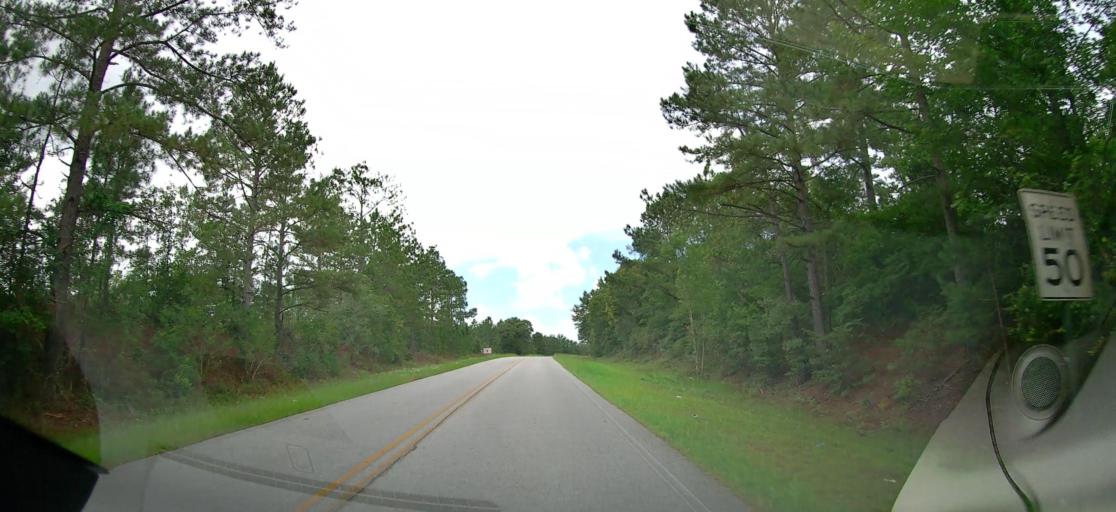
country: US
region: Georgia
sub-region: Peach County
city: Byron
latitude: 32.6916
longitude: -83.7701
